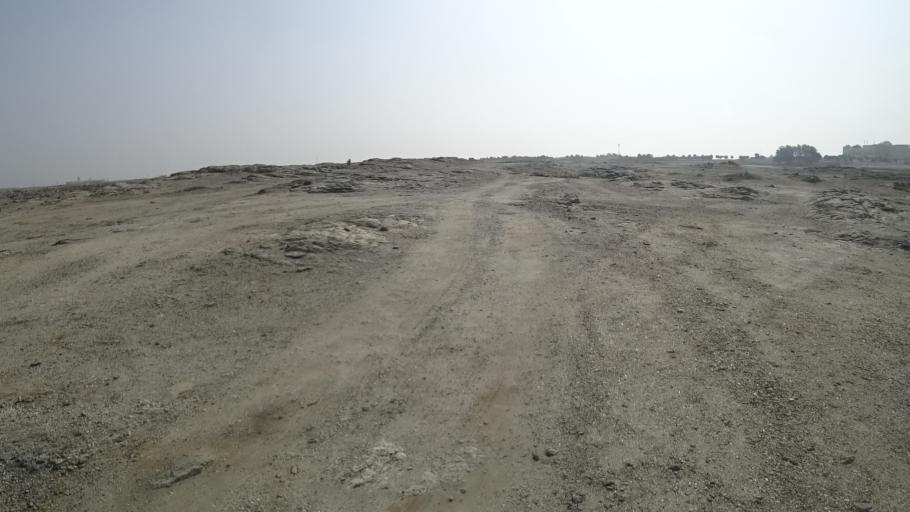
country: OM
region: Zufar
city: Salalah
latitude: 16.9597
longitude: 54.7326
